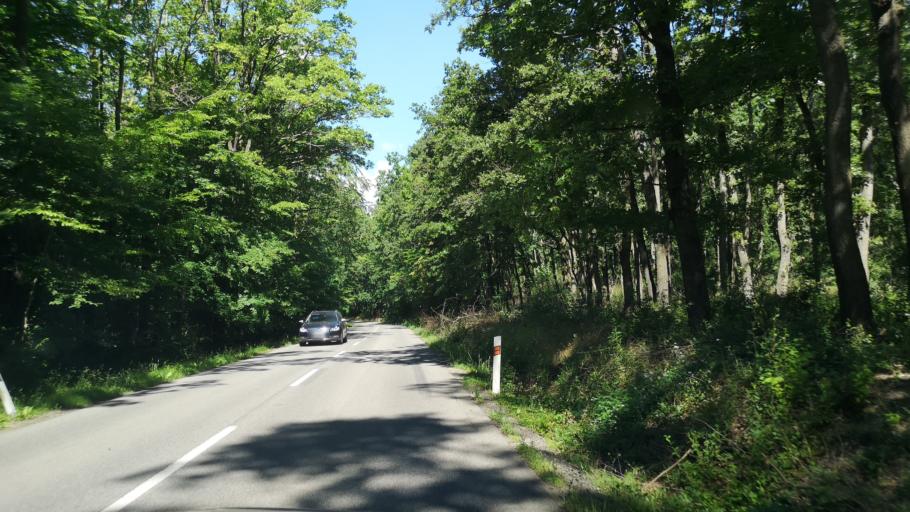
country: SK
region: Nitriansky
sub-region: Okres Nitra
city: Nitra
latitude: 48.2827
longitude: 17.9871
